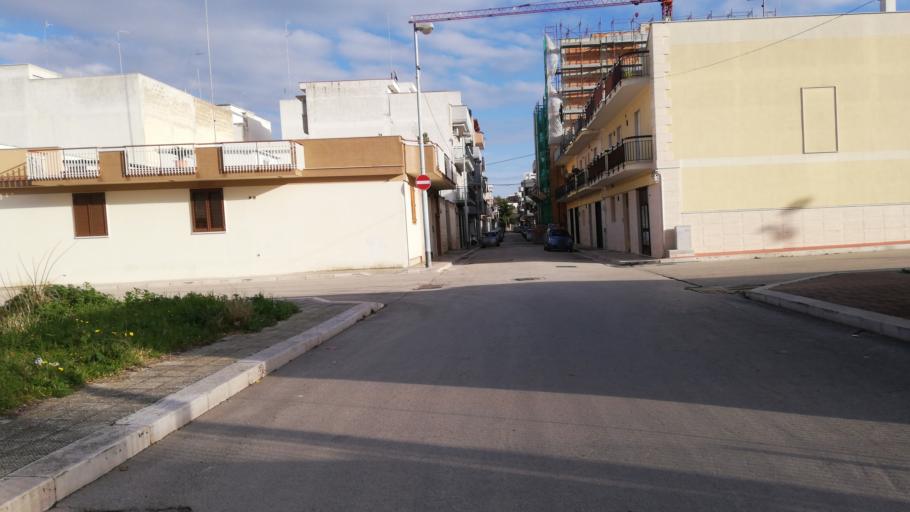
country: IT
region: Apulia
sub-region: Provincia di Barletta - Andria - Trani
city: Andria
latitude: 41.2384
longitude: 16.2962
